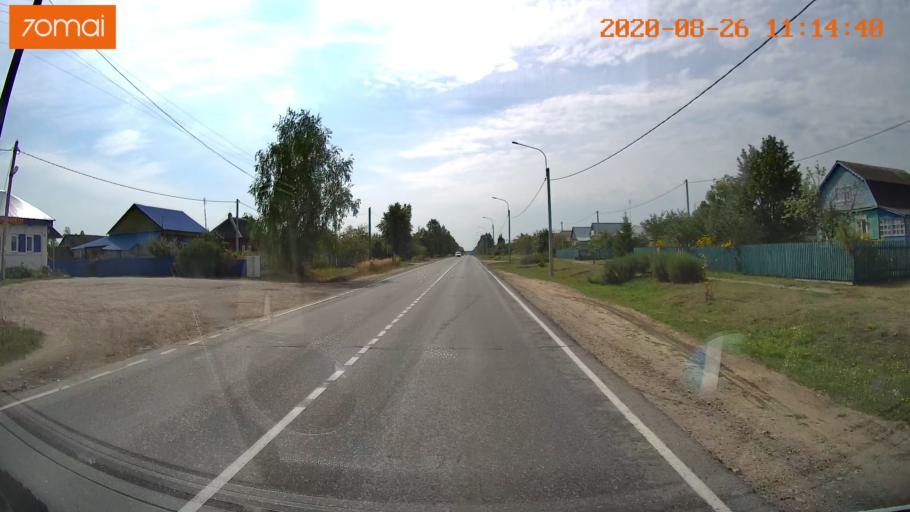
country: RU
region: Rjazan
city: Izhevskoye
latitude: 54.4468
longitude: 41.1164
